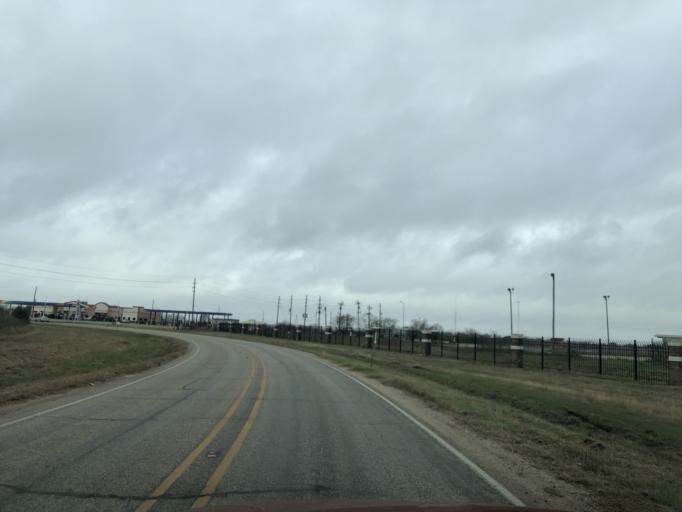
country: US
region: Texas
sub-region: Austin County
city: Sealy
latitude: 29.7608
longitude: -96.2199
